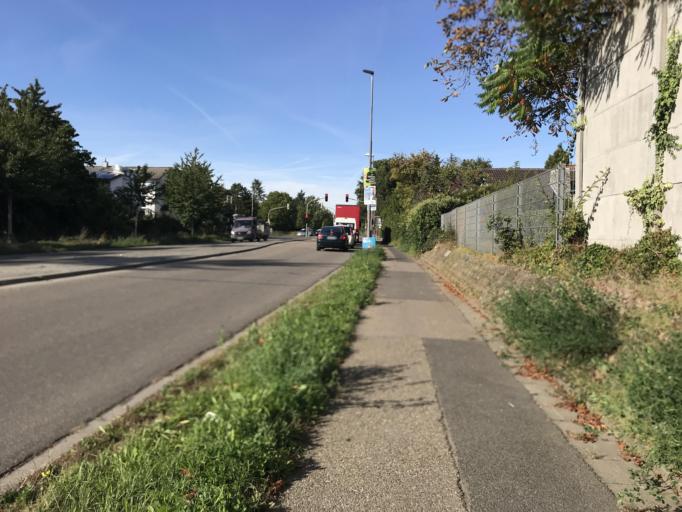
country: DE
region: Rheinland-Pfalz
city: Frankenthal
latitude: 49.5305
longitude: 8.3395
